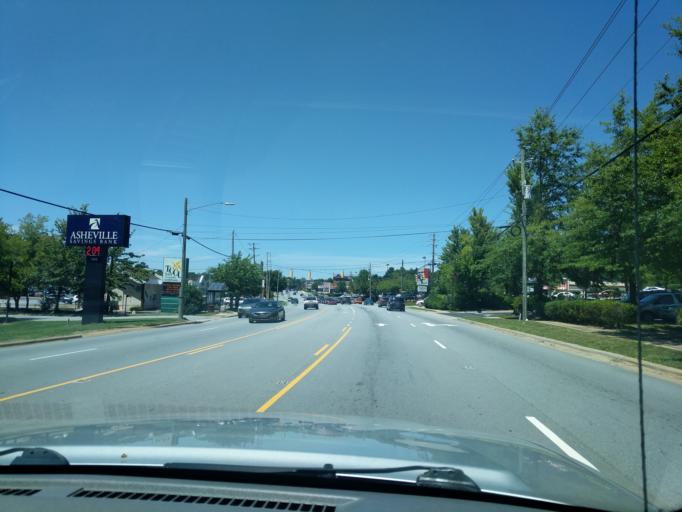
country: US
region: North Carolina
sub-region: Buncombe County
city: Royal Pines
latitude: 35.4989
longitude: -82.5214
